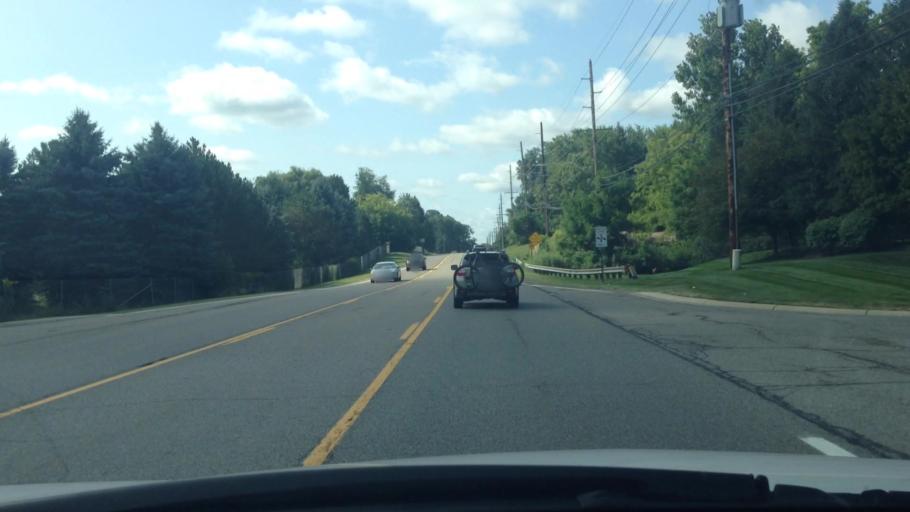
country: US
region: Michigan
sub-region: Oakland County
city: Waterford
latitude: 42.6263
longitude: -83.4425
